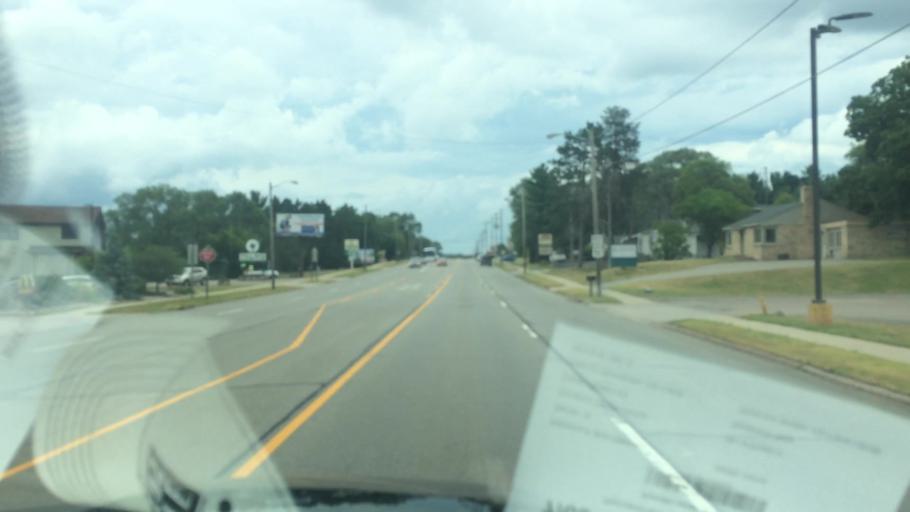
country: US
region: Wisconsin
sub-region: Marathon County
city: Schofield
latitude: 44.9021
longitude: -89.6078
